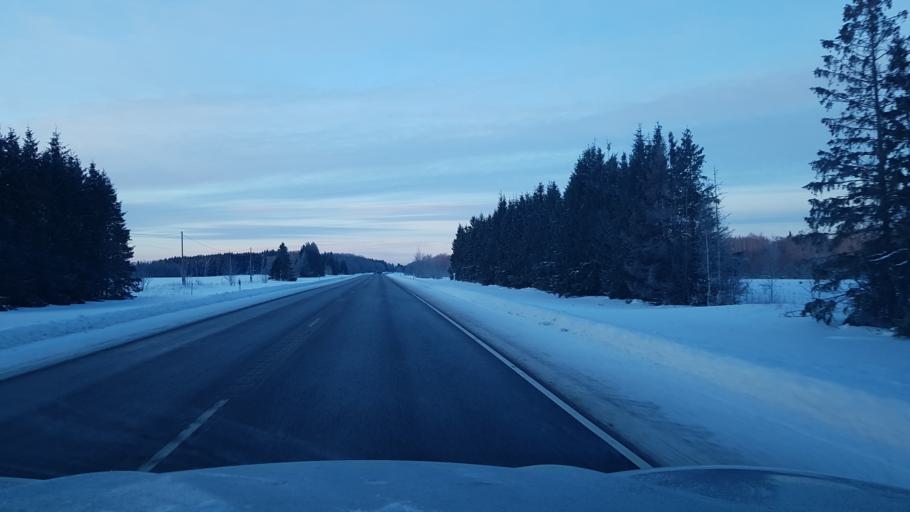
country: EE
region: Ida-Virumaa
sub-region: Narva-Joesuu linn
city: Narva-Joesuu
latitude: 59.3838
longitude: 27.9678
